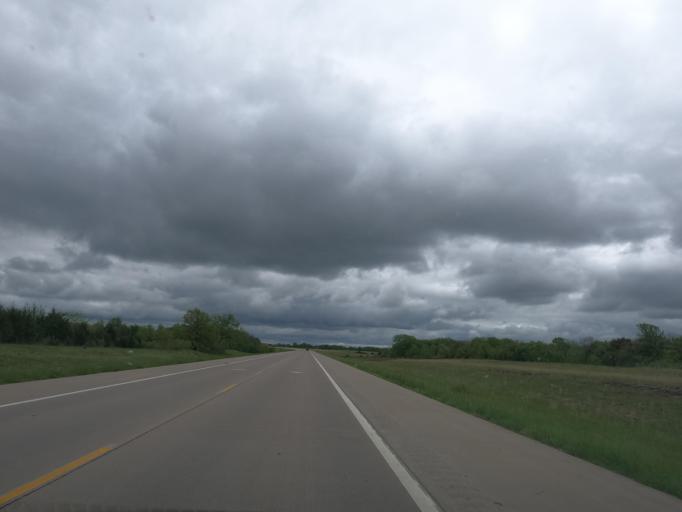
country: US
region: Kansas
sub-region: Labette County
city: Parsons
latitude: 37.3480
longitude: -95.3307
